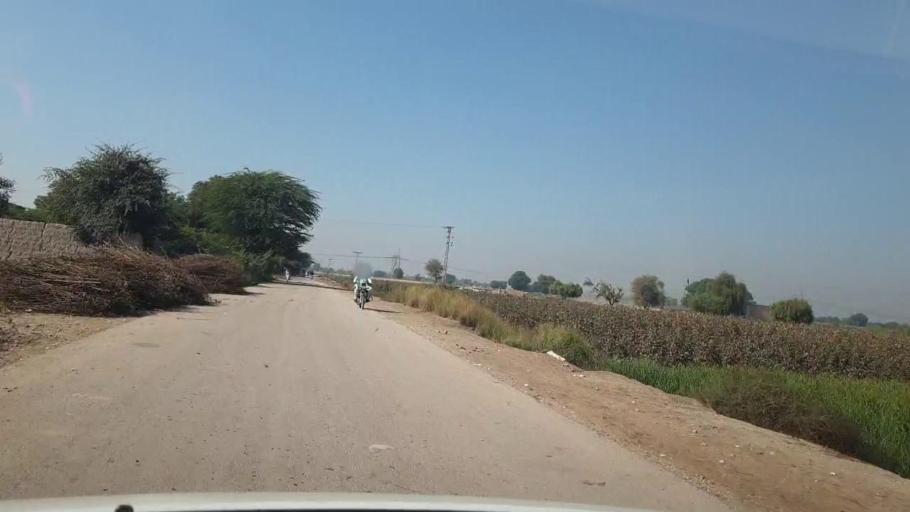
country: PK
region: Sindh
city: Bhan
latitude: 26.6455
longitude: 67.7310
